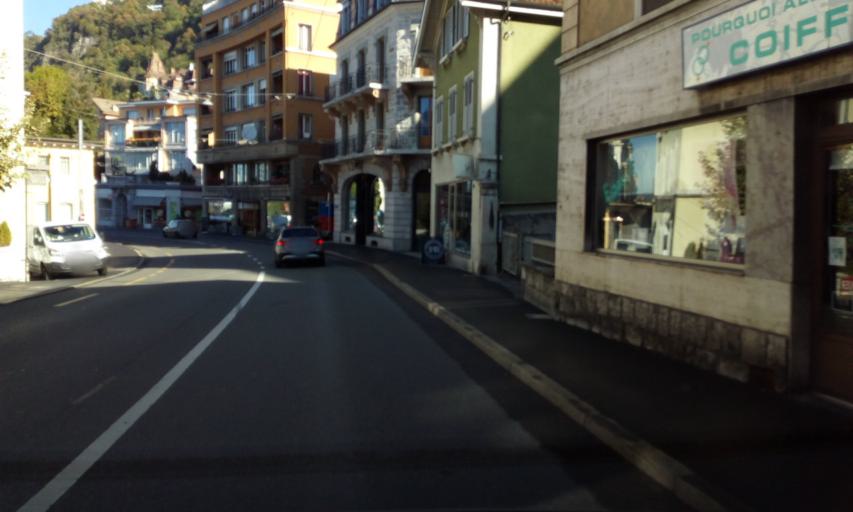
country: CH
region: Vaud
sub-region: Riviera-Pays-d'Enhaut District
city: Caux
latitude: 46.4236
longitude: 6.9256
